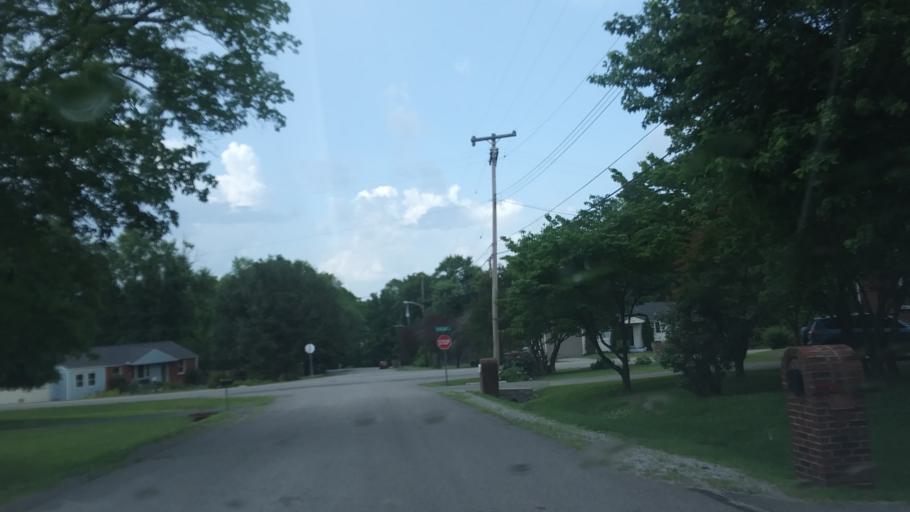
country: US
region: Tennessee
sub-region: Davidson County
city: Oak Hill
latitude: 36.0629
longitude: -86.7071
